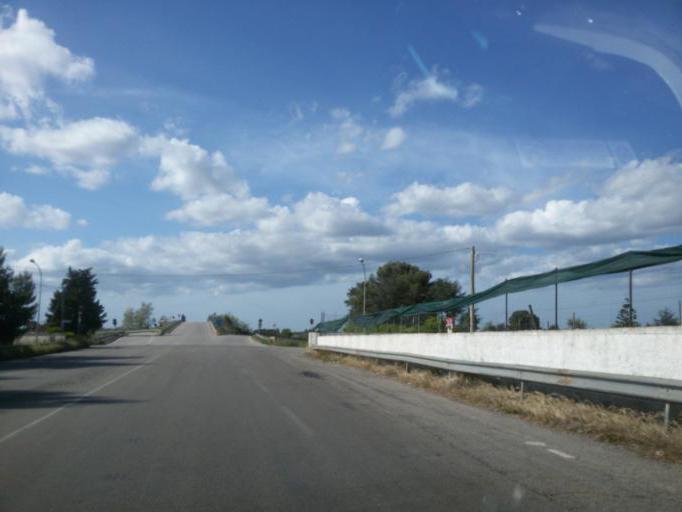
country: IT
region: Apulia
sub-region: Provincia di Brindisi
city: Mesagne
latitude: 40.5657
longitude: 17.7865
